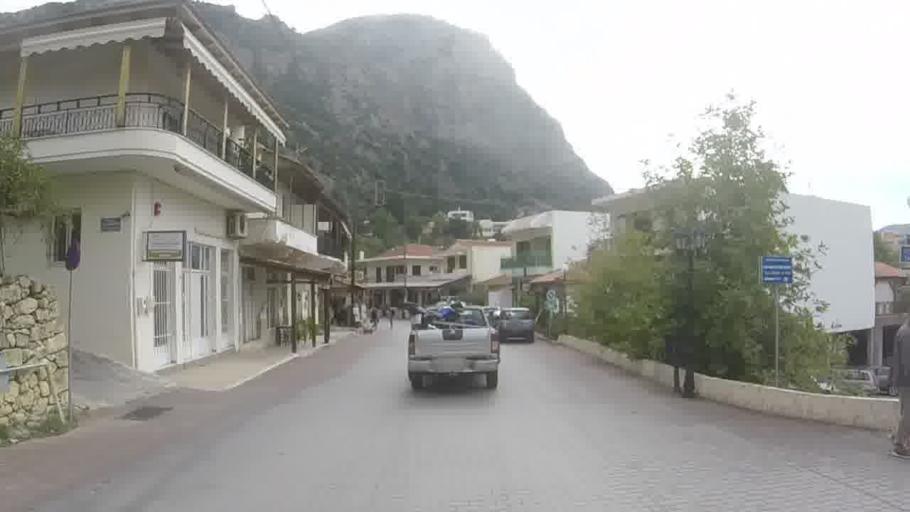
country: GR
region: Crete
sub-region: Nomos Rethymnis
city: Agia Foteini
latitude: 35.2184
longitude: 24.5348
